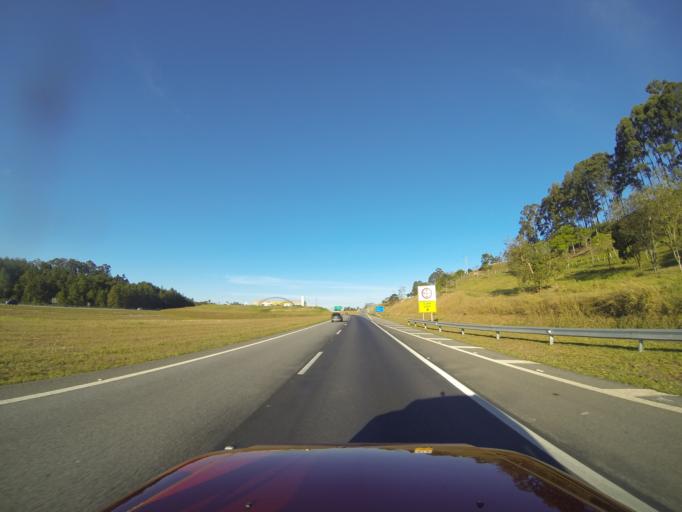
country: BR
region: Sao Paulo
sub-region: Sao Jose Dos Campos
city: Sao Jose dos Campos
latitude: -23.2780
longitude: -45.8483
